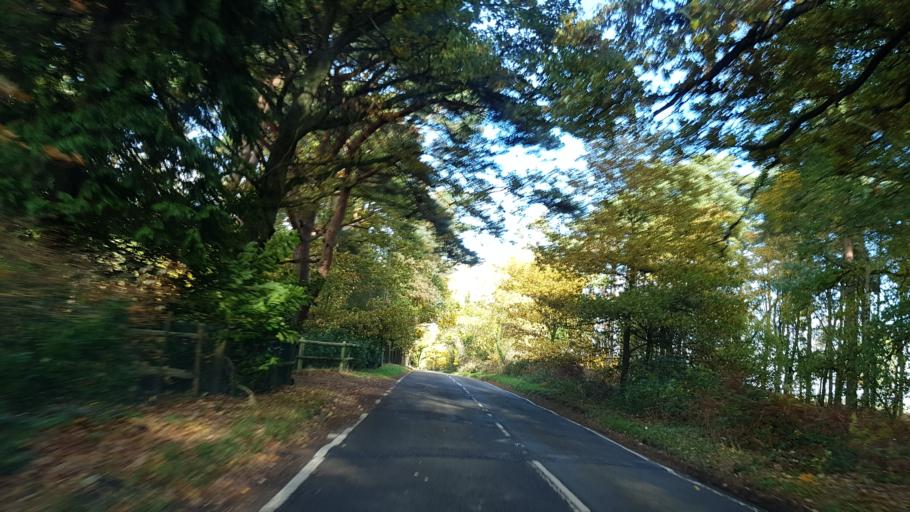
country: GB
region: England
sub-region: Surrey
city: Elstead
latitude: 51.1595
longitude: -0.7174
